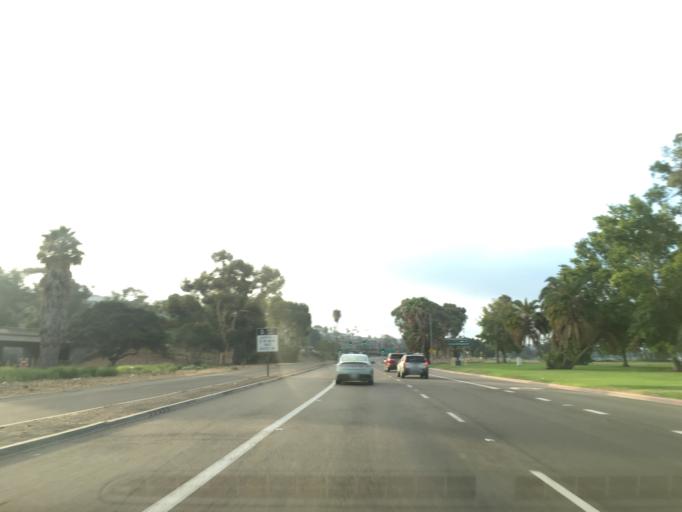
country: US
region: California
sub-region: San Diego County
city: La Jolla
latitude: 32.7996
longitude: -117.2126
